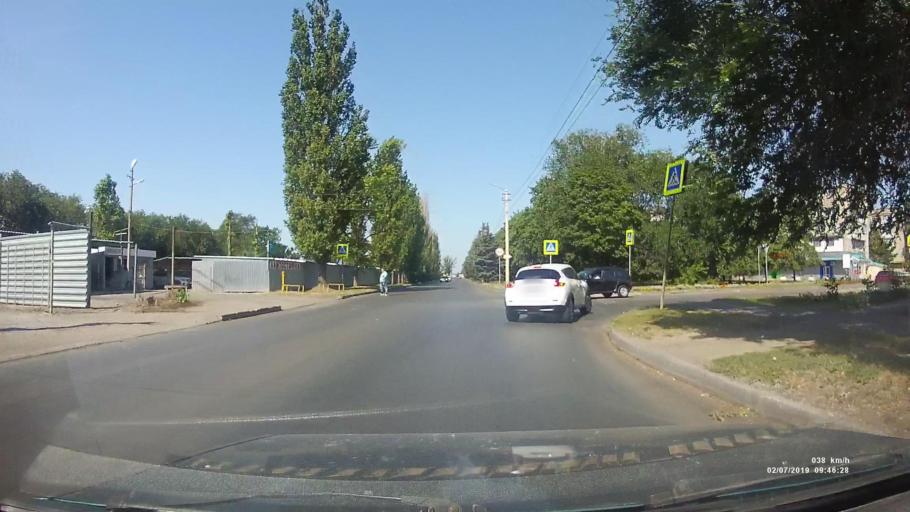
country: RU
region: Rostov
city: Azov
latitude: 47.1018
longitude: 39.4037
